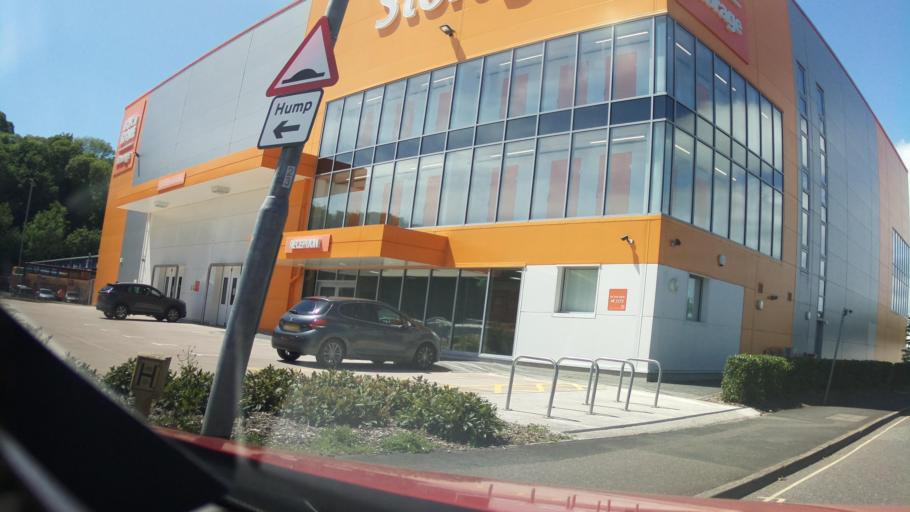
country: GB
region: England
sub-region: Devon
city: Exminster
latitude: 50.6954
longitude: -3.5200
